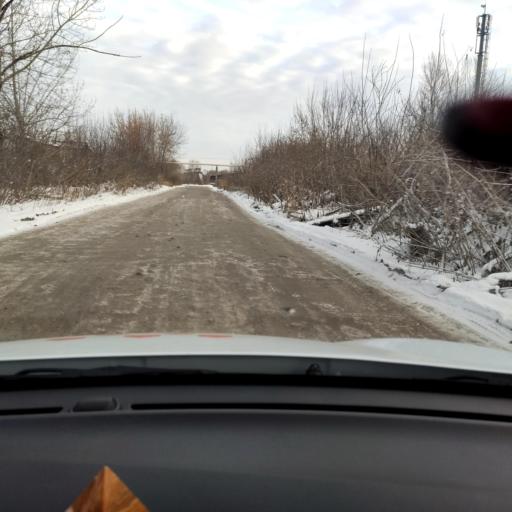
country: RU
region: Tatarstan
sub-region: Gorod Kazan'
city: Kazan
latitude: 55.7394
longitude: 49.1201
